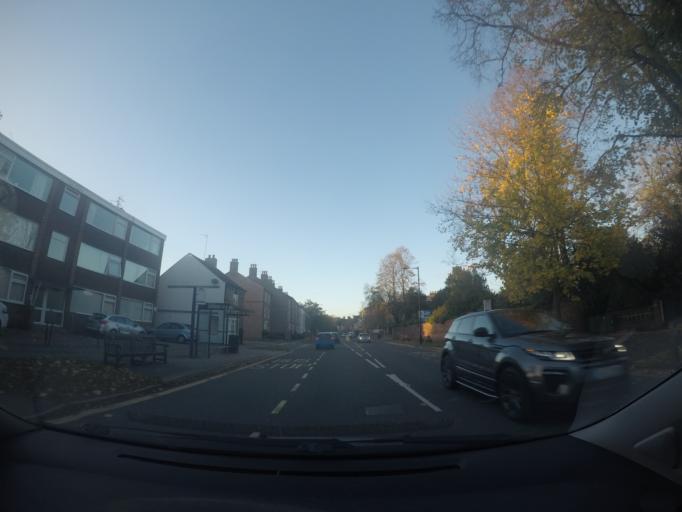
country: GB
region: England
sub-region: City of York
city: Fulford
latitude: 53.9356
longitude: -1.0719
